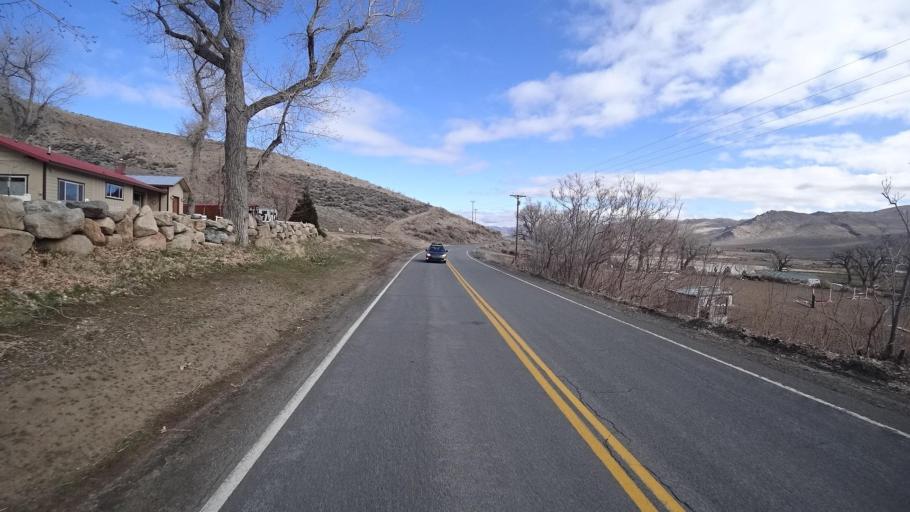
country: US
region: Nevada
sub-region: Washoe County
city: Cold Springs
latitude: 39.8377
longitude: -119.9359
